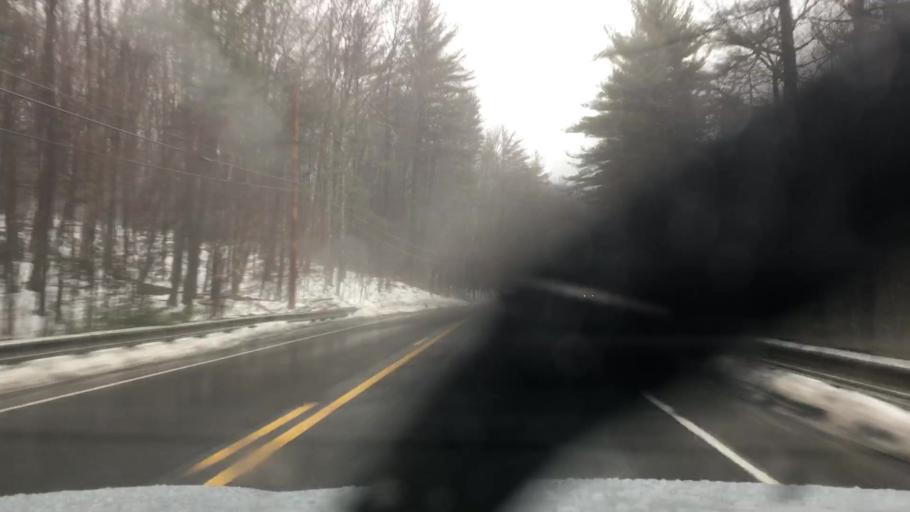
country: US
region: Massachusetts
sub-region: Franklin County
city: Wendell
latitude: 42.5106
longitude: -72.3286
